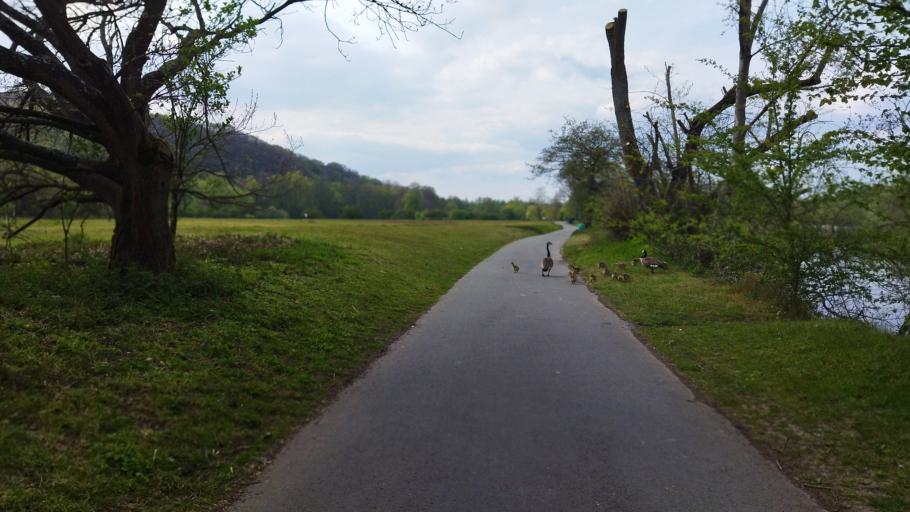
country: DE
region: North Rhine-Westphalia
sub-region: Regierungsbezirk Dusseldorf
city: Essen
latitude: 51.4128
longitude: 7.0751
